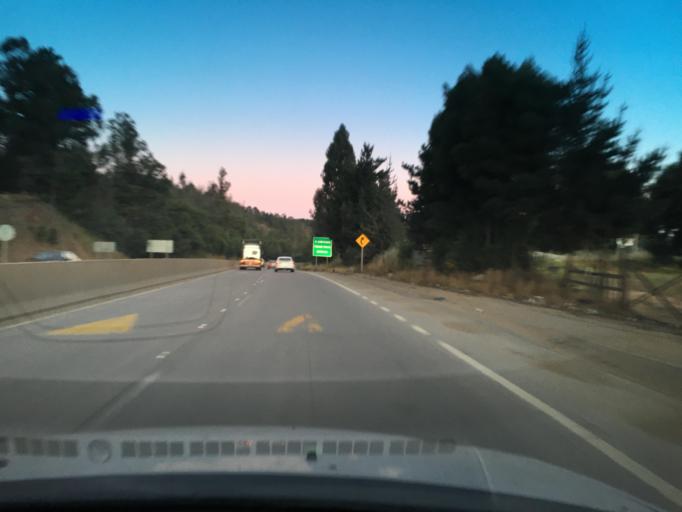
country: CL
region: Valparaiso
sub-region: Provincia de Valparaiso
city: Vina del Mar
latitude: -33.1072
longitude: -71.5678
